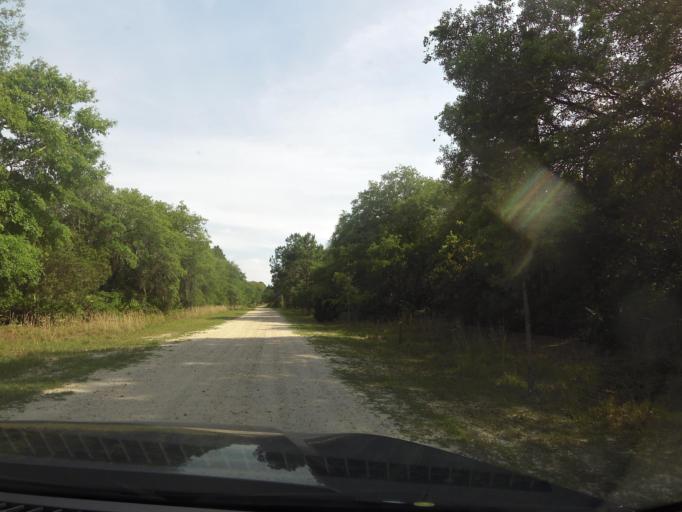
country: US
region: Florida
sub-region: Nassau County
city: Fernandina Beach
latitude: 30.4929
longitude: -81.4910
